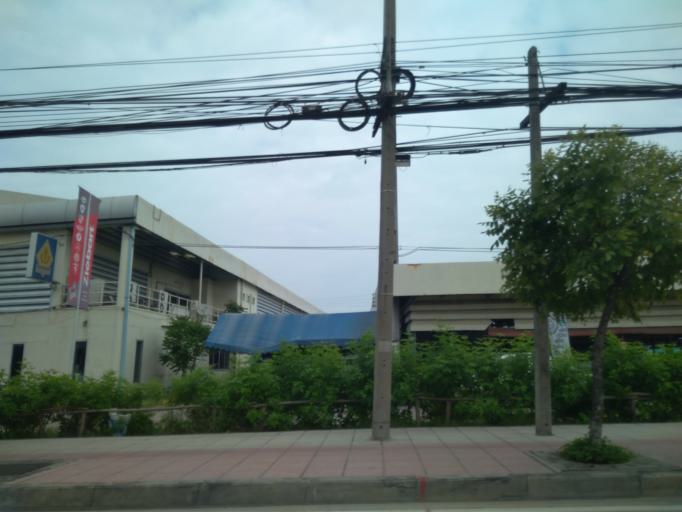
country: TH
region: Bangkok
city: Suan Luang
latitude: 13.7193
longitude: 100.6424
